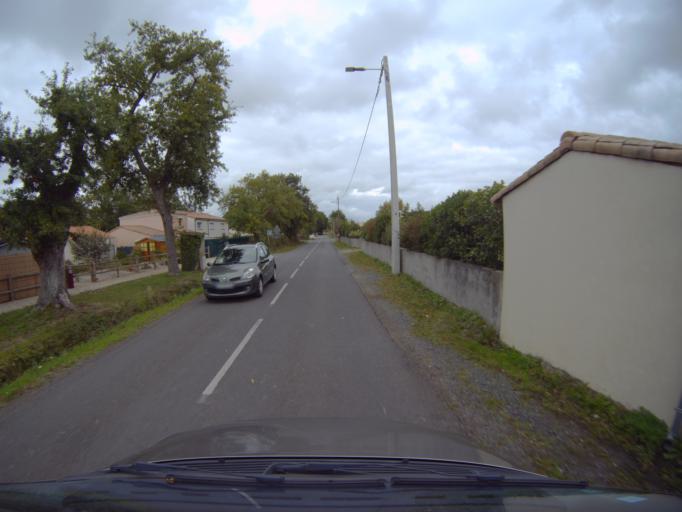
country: FR
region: Pays de la Loire
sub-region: Departement de la Loire-Atlantique
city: Clisson
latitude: 47.1029
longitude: -1.2666
